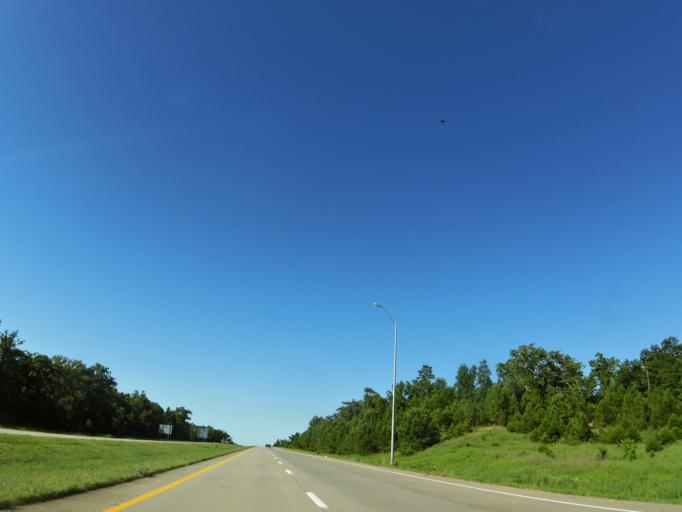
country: US
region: Missouri
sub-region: Butler County
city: Poplar Bluff
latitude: 36.7838
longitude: -90.4521
